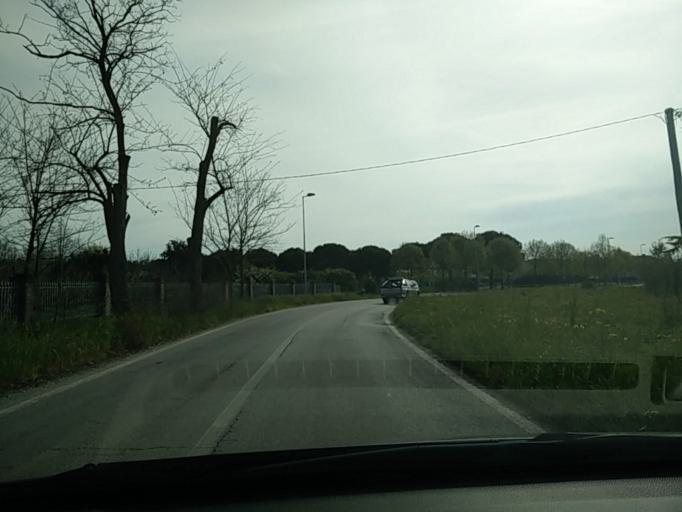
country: IT
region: Emilia-Romagna
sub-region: Provincia di Rimini
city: Santa Giustina
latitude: 44.0816
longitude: 12.5001
